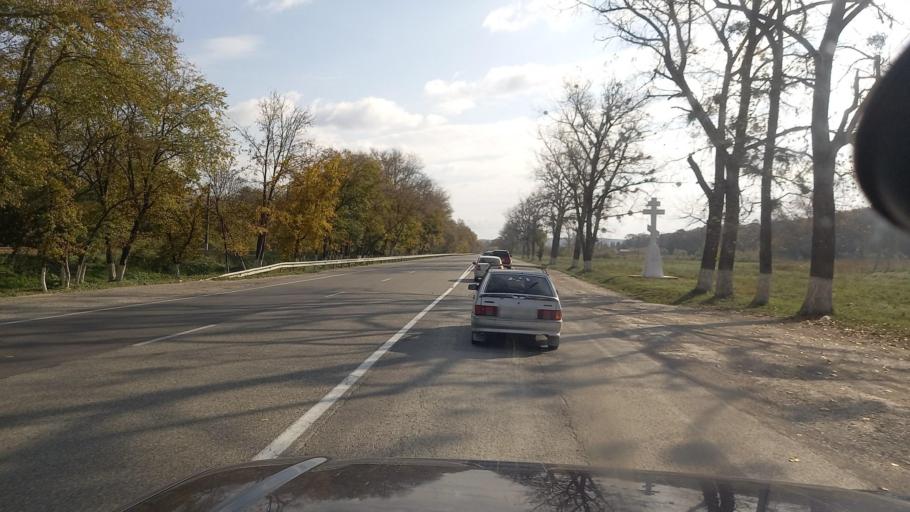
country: RU
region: Krasnodarskiy
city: Gayduk
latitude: 44.8728
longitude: 37.8302
